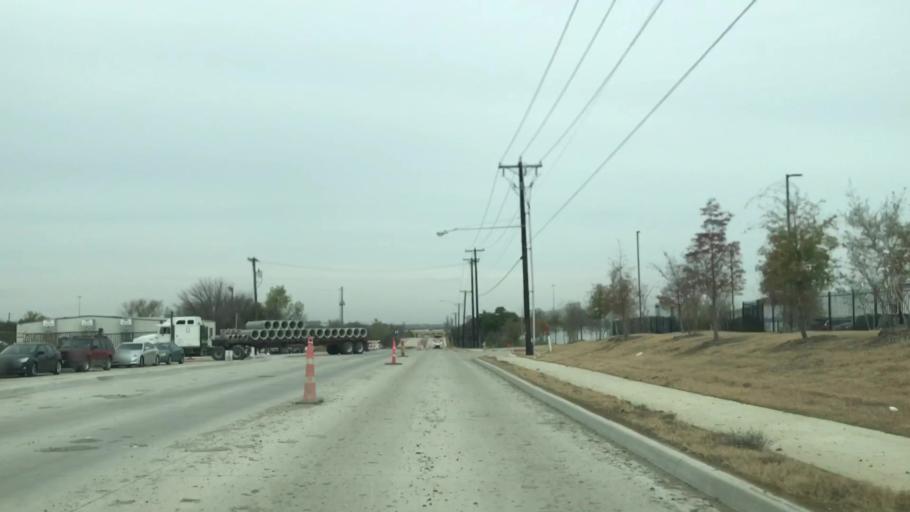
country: US
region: Texas
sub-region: Dallas County
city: Cockrell Hill
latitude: 32.7578
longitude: -96.9021
